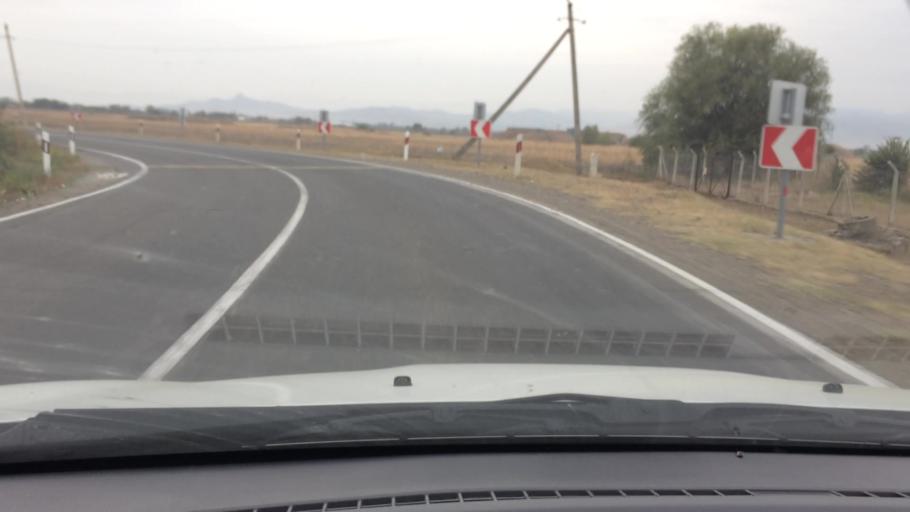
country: GE
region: Kvemo Kartli
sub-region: Marneuli
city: Marneuli
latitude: 41.4663
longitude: 44.8042
